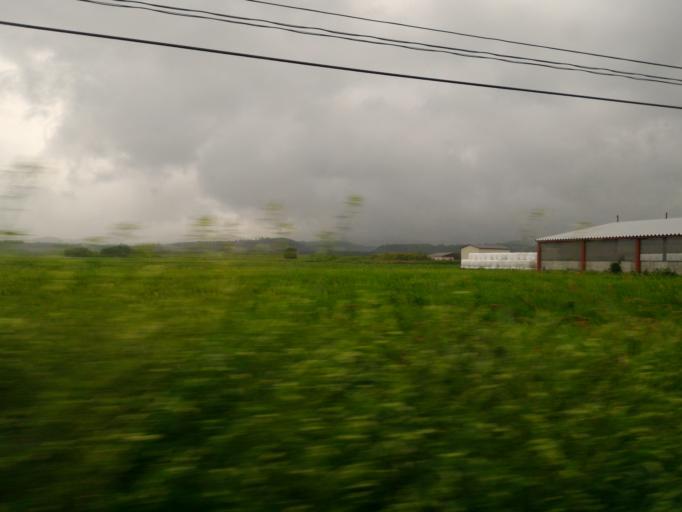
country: JP
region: Hokkaido
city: Makubetsu
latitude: 44.8256
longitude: 142.0636
